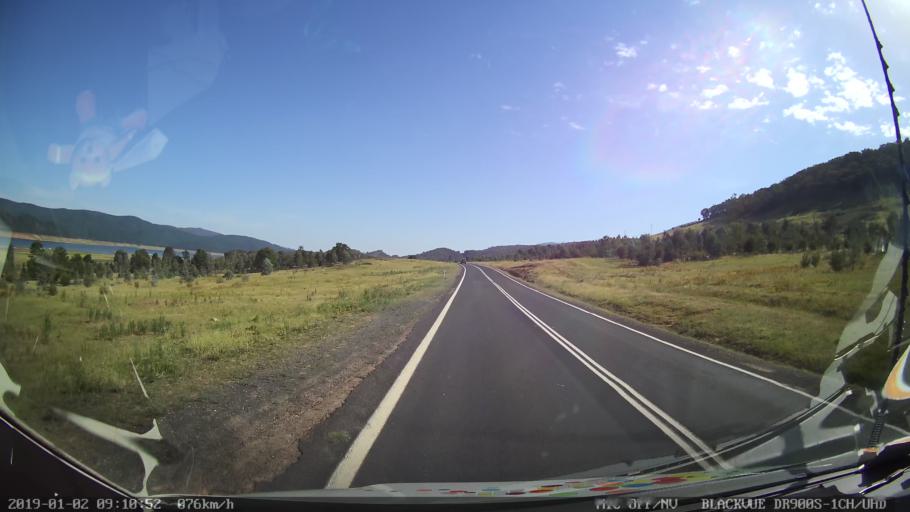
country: AU
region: New South Wales
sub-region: Tumut Shire
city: Tumut
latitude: -35.5177
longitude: 148.2685
